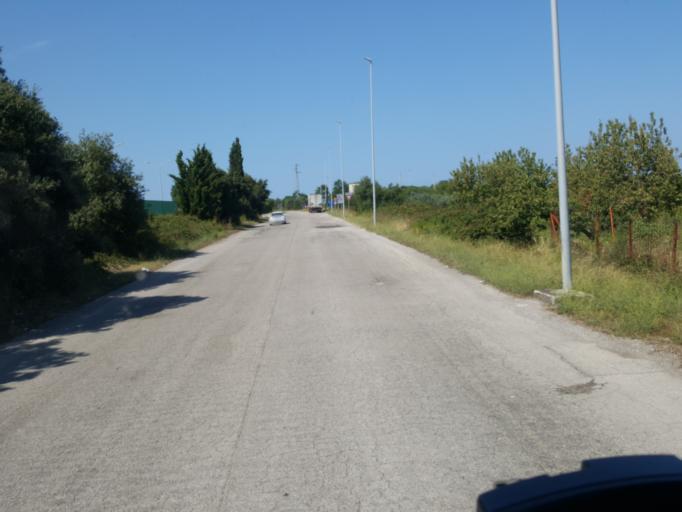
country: IT
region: Abruzzo
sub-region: Provincia di Chieti
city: Salvo Marina
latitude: 42.0640
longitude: 14.7622
